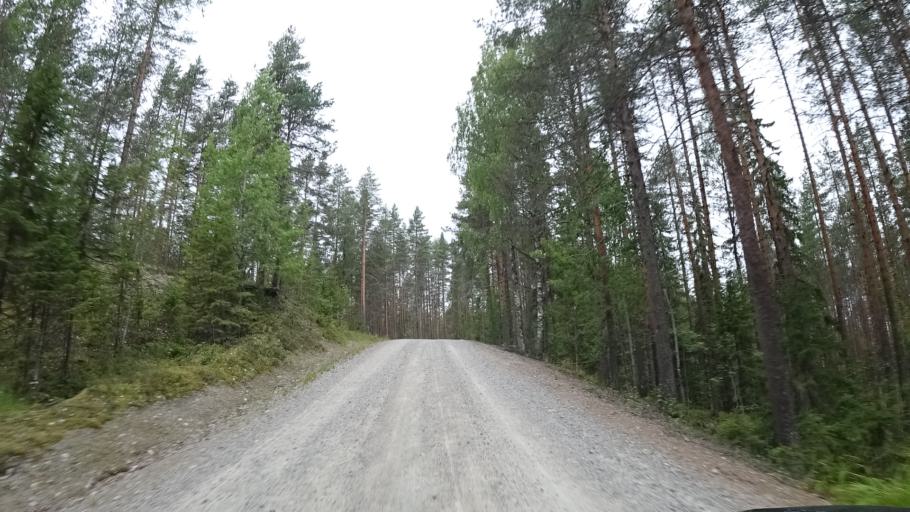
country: FI
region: North Karelia
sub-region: Pielisen Karjala
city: Lieksa
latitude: 63.2081
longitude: 30.4216
